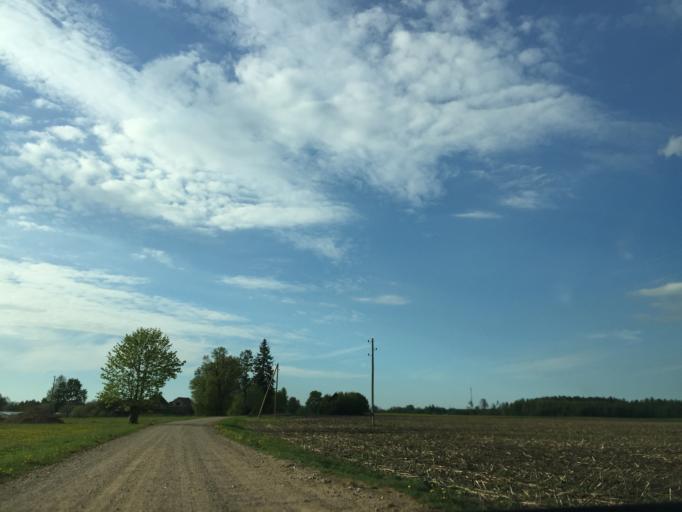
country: LV
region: Limbazu Rajons
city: Limbazi
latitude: 57.3641
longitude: 24.6945
